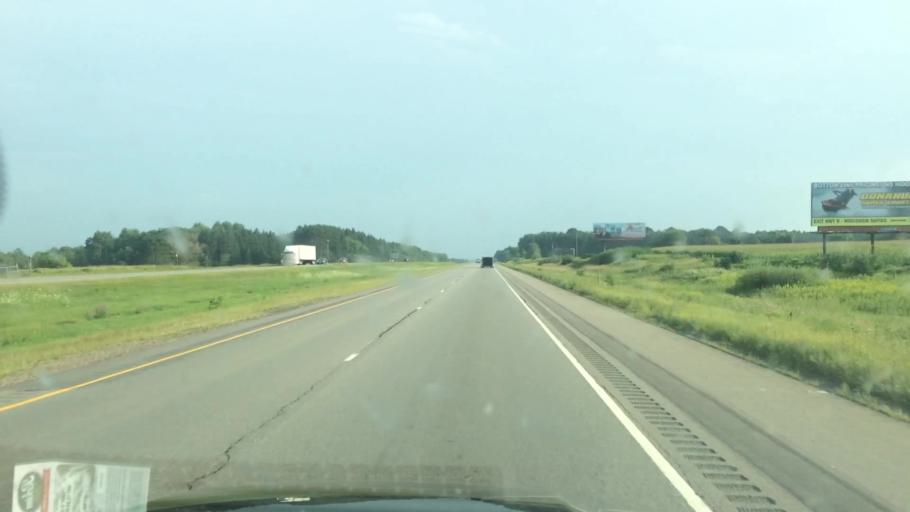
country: US
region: Wisconsin
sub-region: Marathon County
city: Mosinee
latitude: 44.7749
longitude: -89.6805
